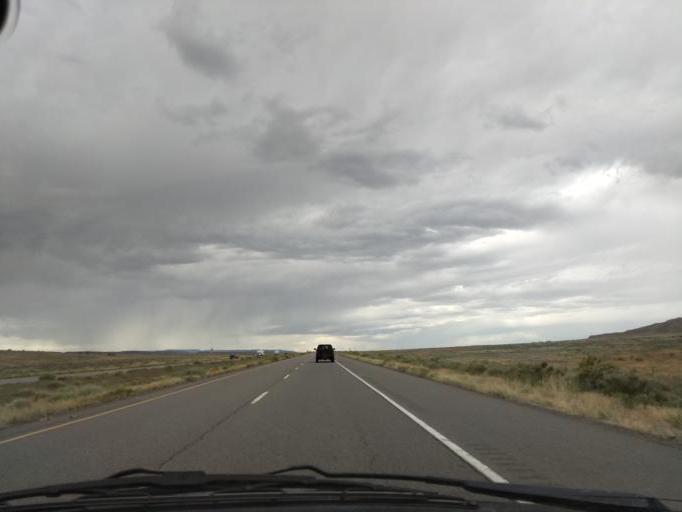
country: US
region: Colorado
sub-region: Delta County
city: Delta
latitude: 38.7792
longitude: -108.2367
